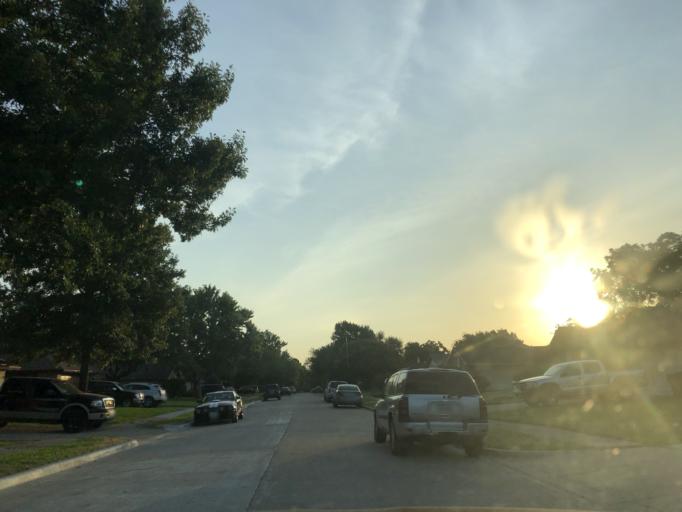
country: US
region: Texas
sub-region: Dallas County
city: Garland
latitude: 32.8603
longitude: -96.6330
